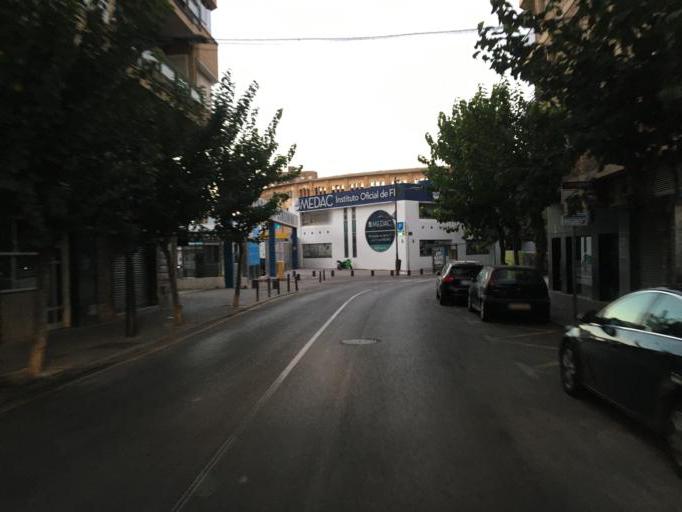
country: ES
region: Murcia
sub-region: Murcia
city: Murcia
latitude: 37.9866
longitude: -1.1230
